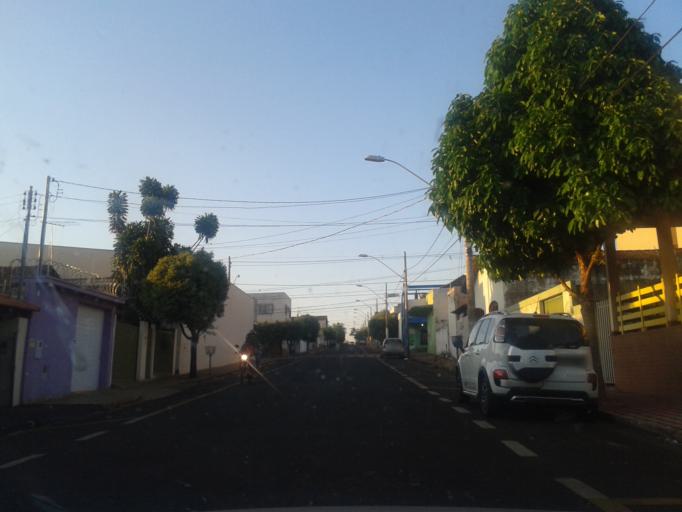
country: BR
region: Minas Gerais
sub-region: Ituiutaba
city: Ituiutaba
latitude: -18.9736
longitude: -49.4581
